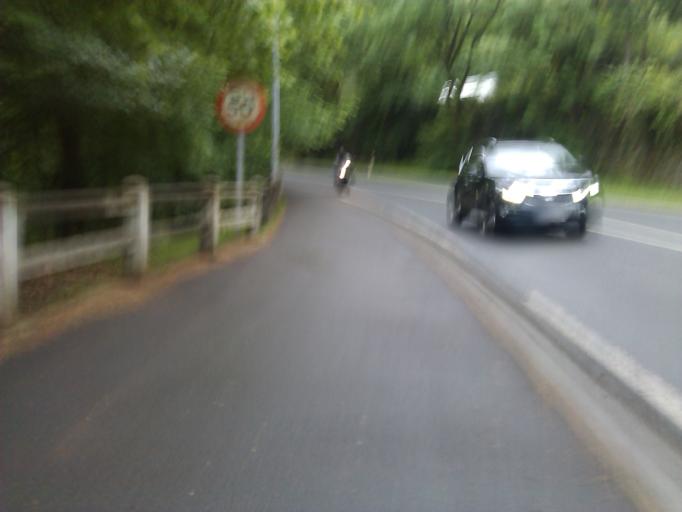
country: ES
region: Basque Country
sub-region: Provincia de Guipuzcoa
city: San Sebastian
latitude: 43.3060
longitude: -1.9660
